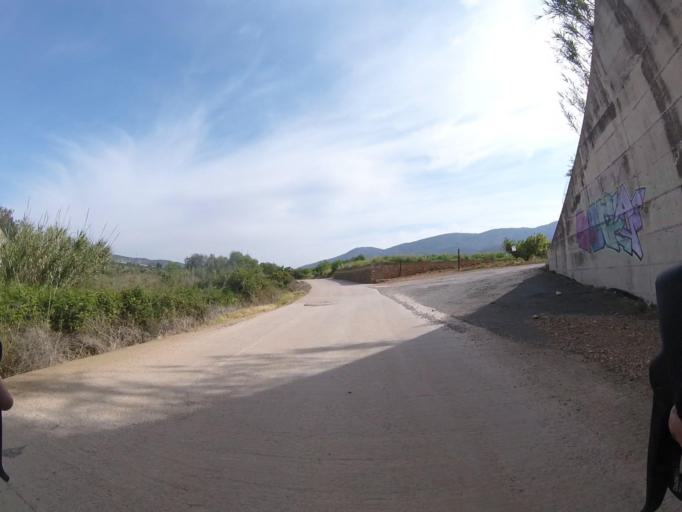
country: ES
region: Valencia
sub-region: Provincia de Castello
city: Alcoceber
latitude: 40.2687
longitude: 0.2522
